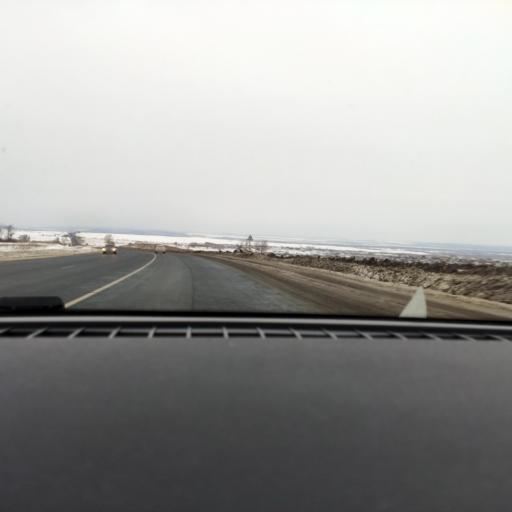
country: RU
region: Samara
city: Novosemeykino
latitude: 53.3980
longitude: 50.4221
